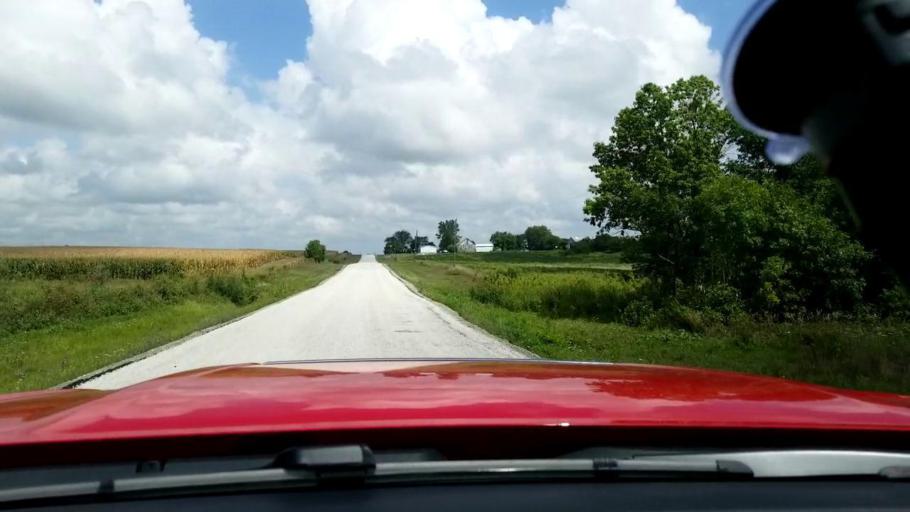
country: US
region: Iowa
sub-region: Decatur County
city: Lamoni
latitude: 40.6344
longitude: -94.0530
